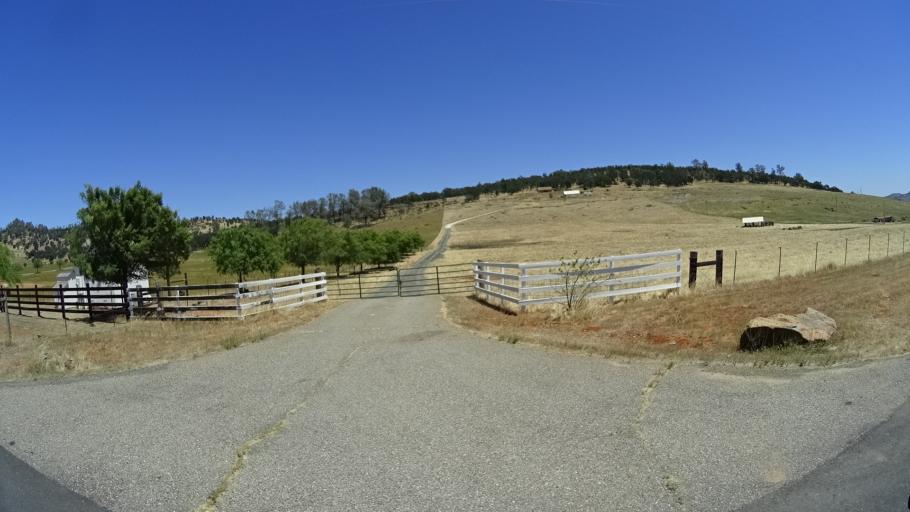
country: US
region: California
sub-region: Calaveras County
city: Copperopolis
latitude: 37.9795
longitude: -120.6646
